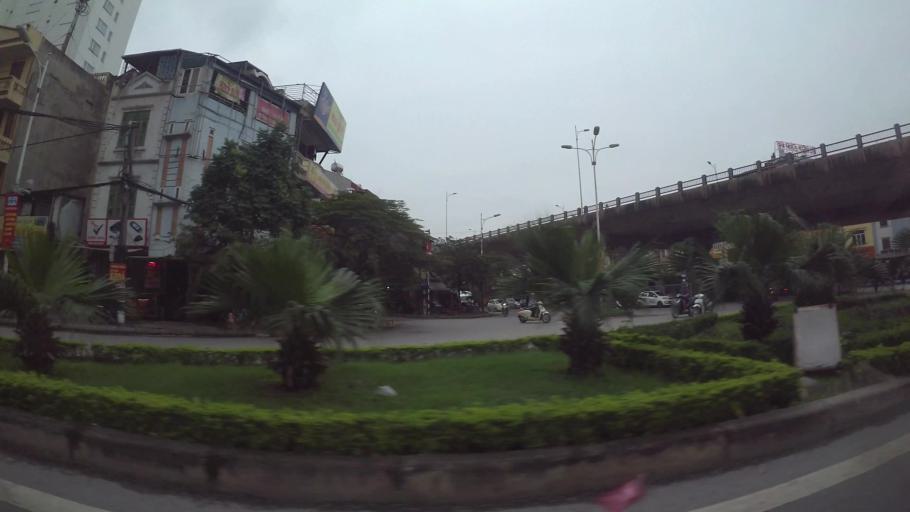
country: VN
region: Ha Noi
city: Hai BaTrung
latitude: 21.0000
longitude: 105.8710
